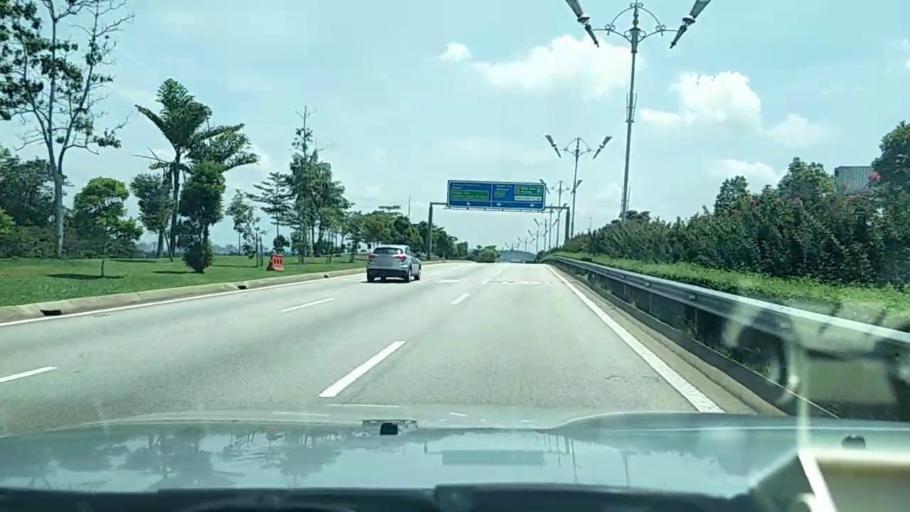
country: MY
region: Putrajaya
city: Putrajaya
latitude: 2.9571
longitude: 101.7072
